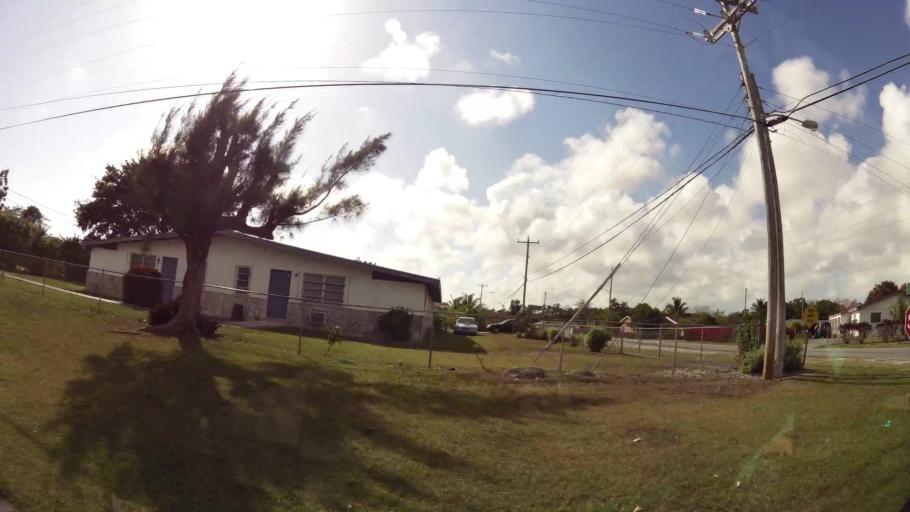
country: BS
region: Freeport
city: Freeport
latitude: 26.5215
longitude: -78.6867
